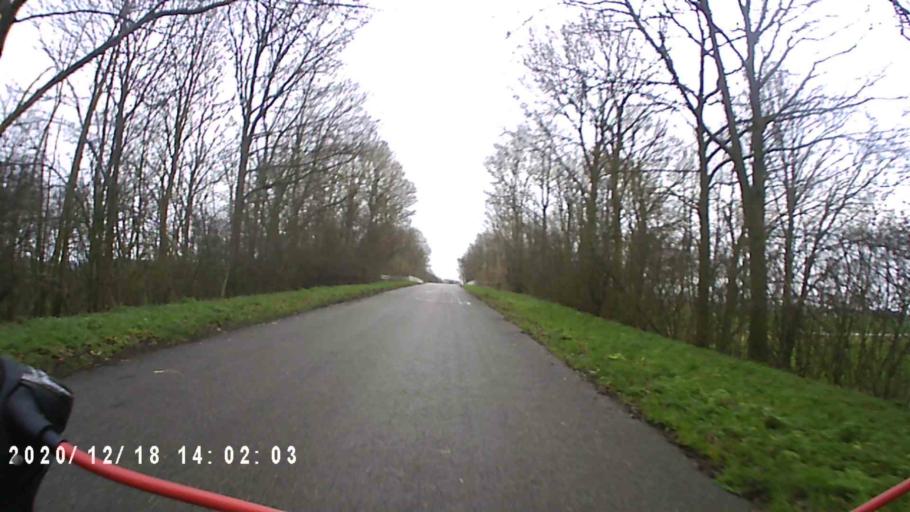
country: NL
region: Groningen
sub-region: Gemeente Bedum
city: Bedum
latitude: 53.2949
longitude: 6.6439
